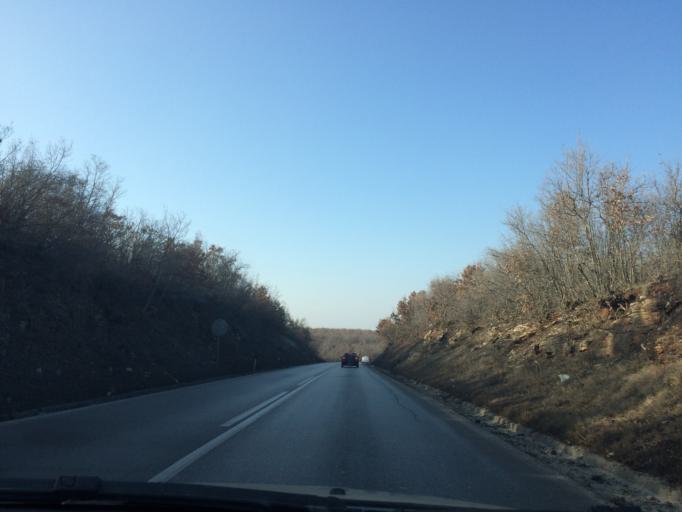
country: XK
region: Pec
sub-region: Komuna e Klines
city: Klina
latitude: 42.5959
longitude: 20.6158
